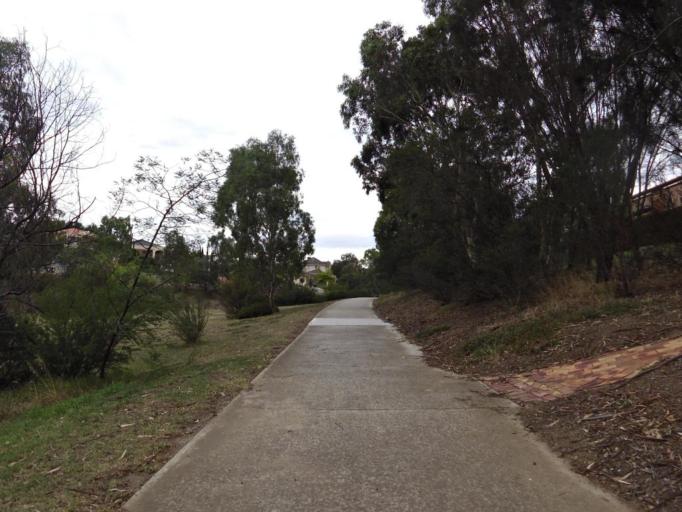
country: AU
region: Victoria
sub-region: Hume
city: Westmeadows
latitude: -37.6727
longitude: 144.8948
